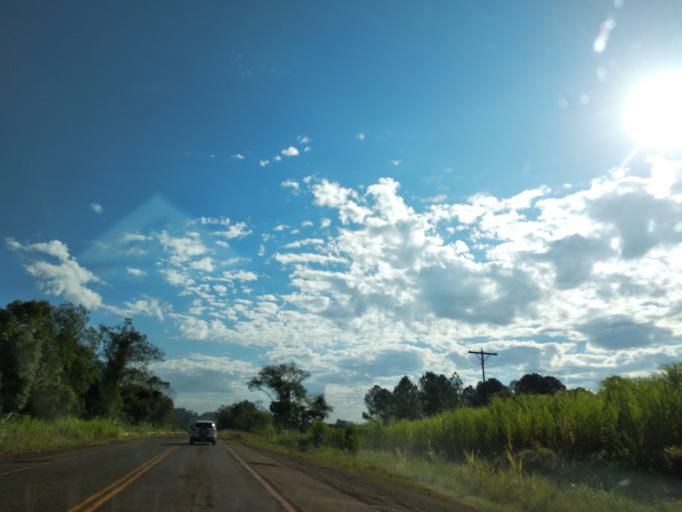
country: AR
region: Misiones
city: Ruiz de Montoya
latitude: -27.0590
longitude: -55.0244
